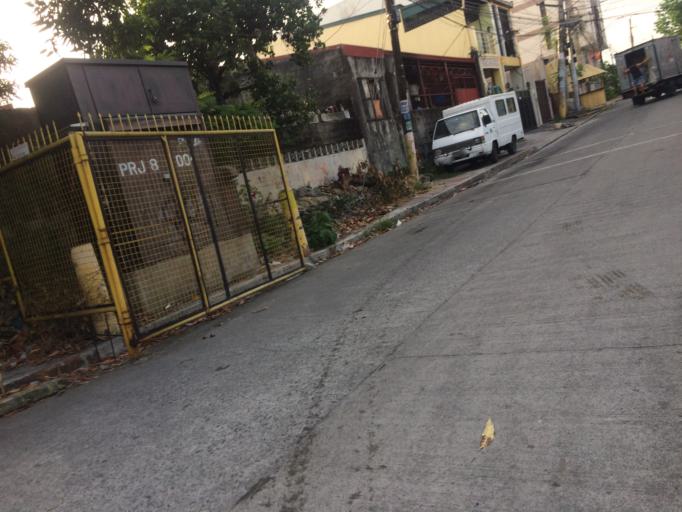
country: PH
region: Calabarzon
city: Bagong Pagasa
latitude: 14.6716
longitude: 121.0174
